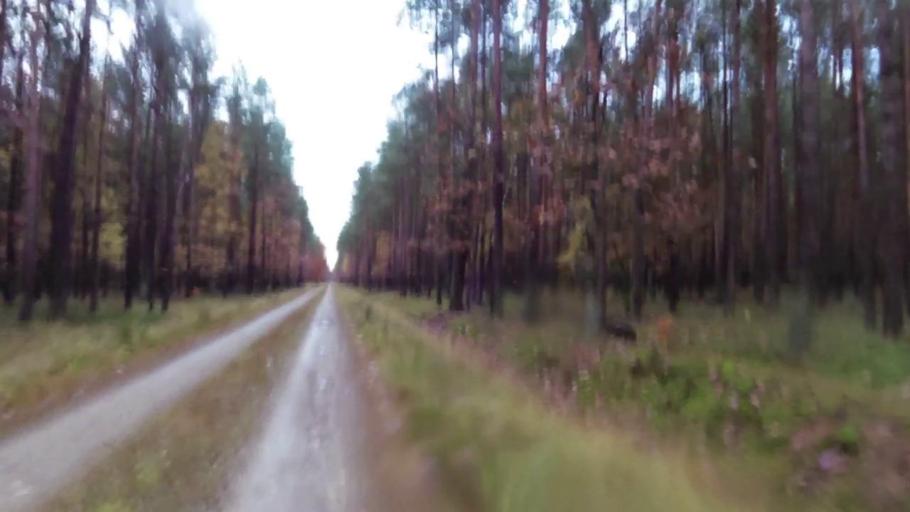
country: PL
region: West Pomeranian Voivodeship
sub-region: Powiat goleniowski
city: Stepnica
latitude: 53.6432
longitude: 14.7040
